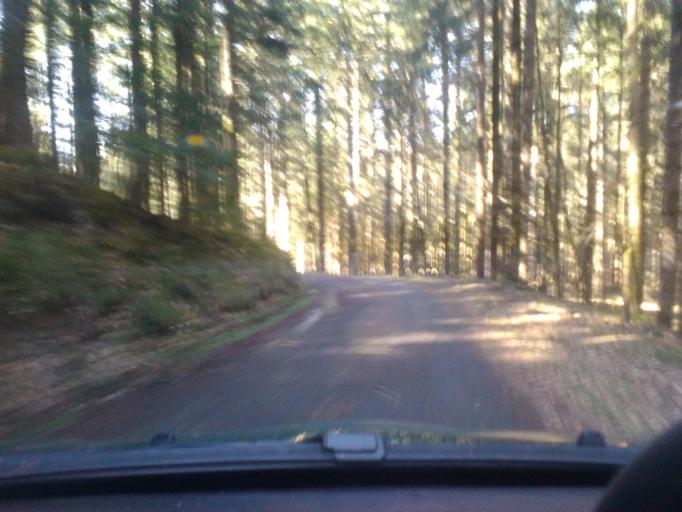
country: FR
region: Lorraine
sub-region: Departement des Vosges
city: Xonrupt-Longemer
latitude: 48.0818
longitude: 6.9606
